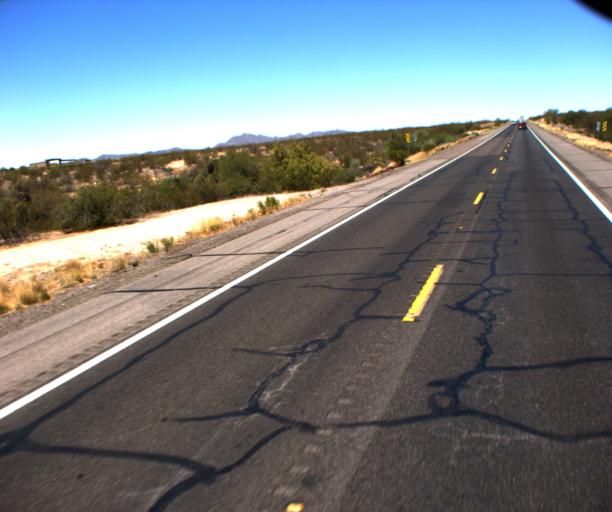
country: US
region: Arizona
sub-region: Yavapai County
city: Congress
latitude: 34.0444
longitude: -112.8370
